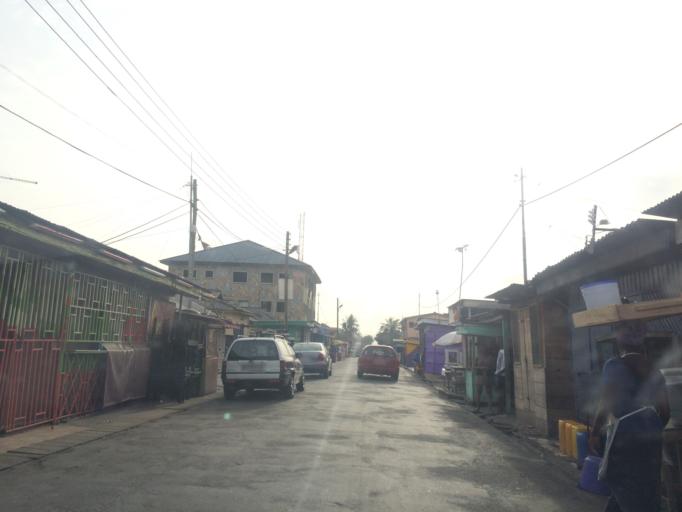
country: GH
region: Greater Accra
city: Accra
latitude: 5.5425
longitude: -0.2132
